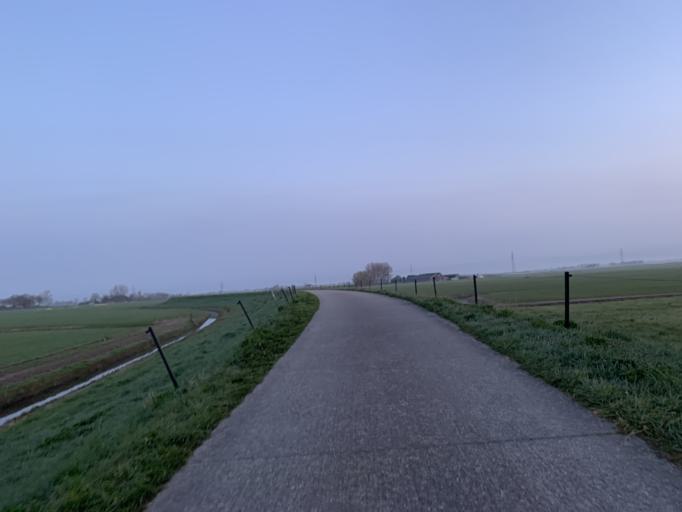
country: NL
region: Groningen
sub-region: Gemeente Zuidhorn
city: Aduard
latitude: 53.2766
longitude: 6.5087
